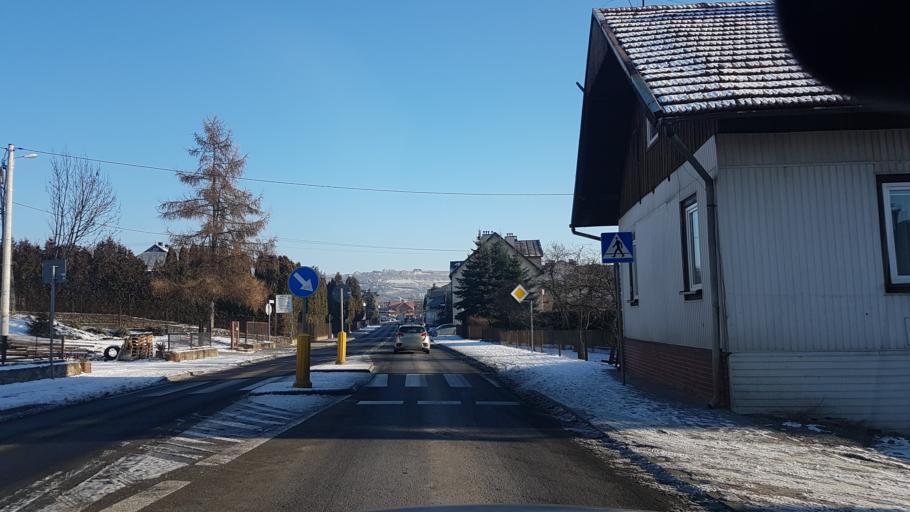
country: PL
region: Lesser Poland Voivodeship
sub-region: Powiat nowosadecki
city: Lacko
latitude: 49.5558
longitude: 20.4322
